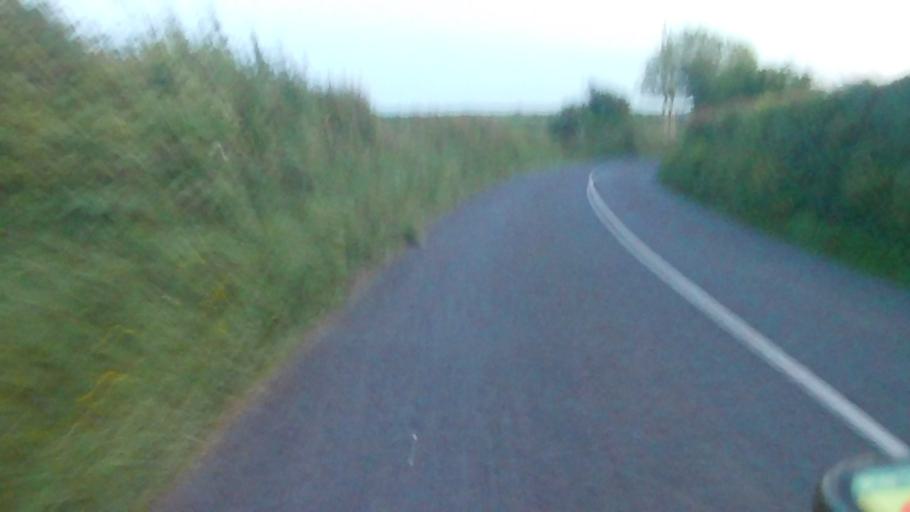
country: IE
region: Munster
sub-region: County Cork
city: Carrigtwohill
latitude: 51.9485
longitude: -8.3026
